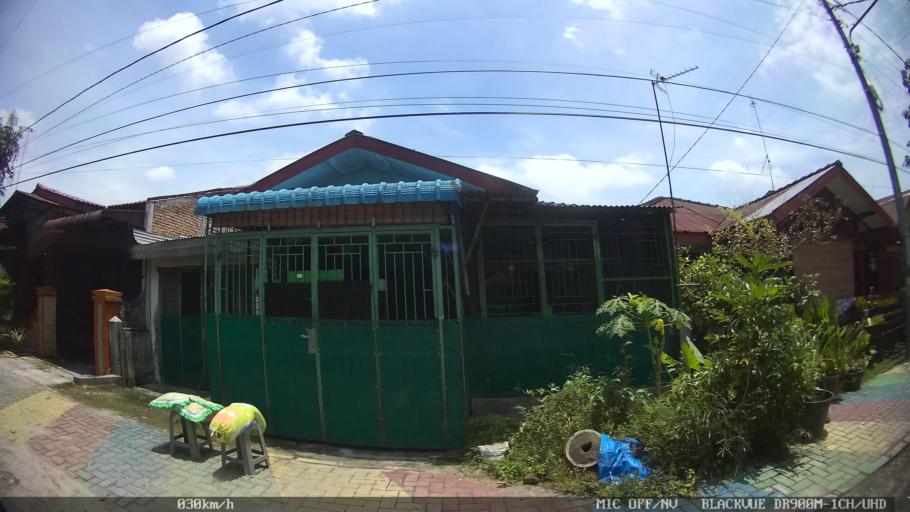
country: ID
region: North Sumatra
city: Percut
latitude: 3.5433
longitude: 98.8754
